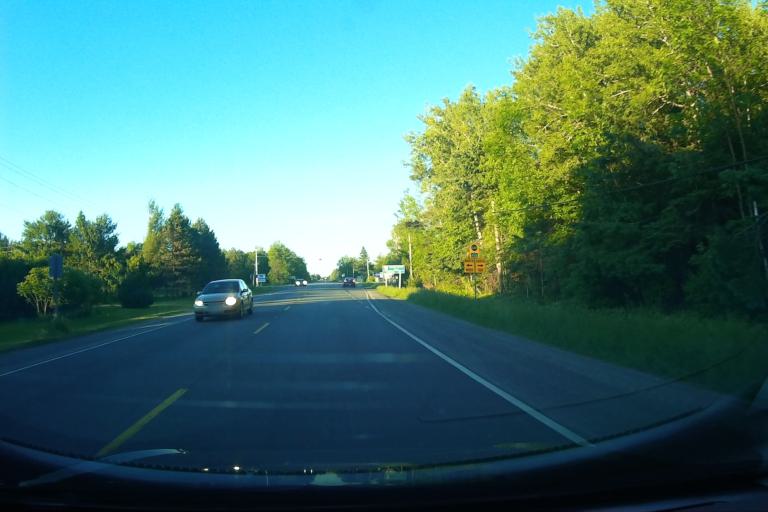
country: CA
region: Ontario
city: Prescott
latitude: 45.0387
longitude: -75.5938
